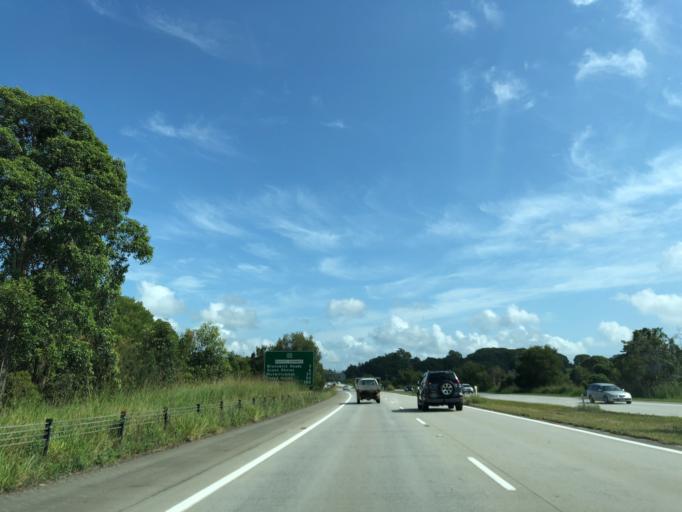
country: AU
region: New South Wales
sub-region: Byron Shire
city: Brunswick Heads
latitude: -28.5791
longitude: 153.5440
